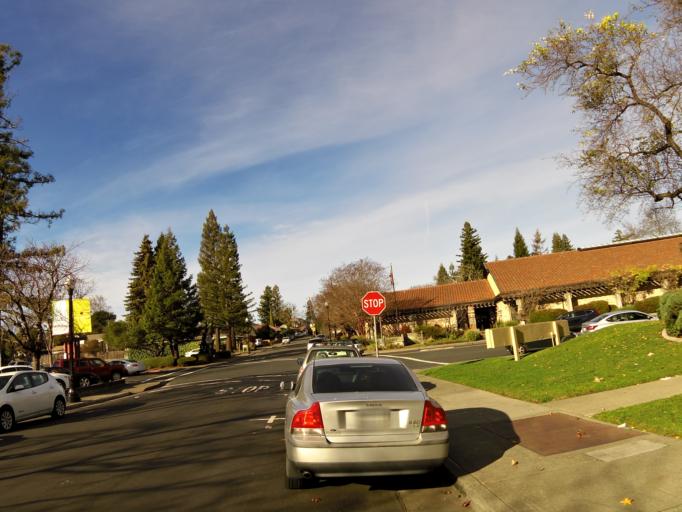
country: US
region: California
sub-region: Sonoma County
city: Healdsburg
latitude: 38.6139
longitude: -122.8703
